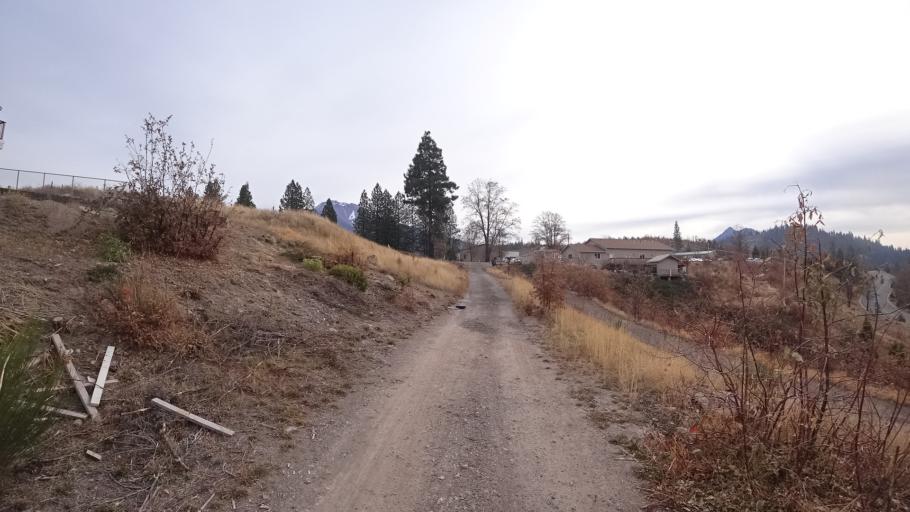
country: US
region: California
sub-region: Siskiyou County
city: Weed
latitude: 41.4292
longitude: -122.3824
